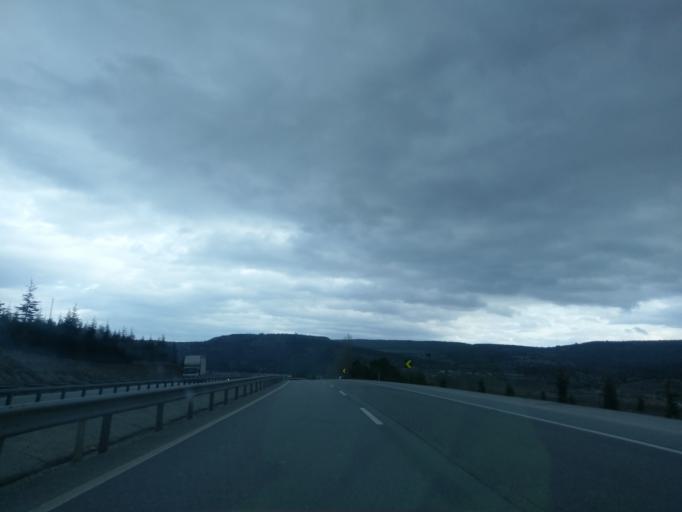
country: TR
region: Kuetahya
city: Sabuncu
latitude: 39.5708
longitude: 30.1111
